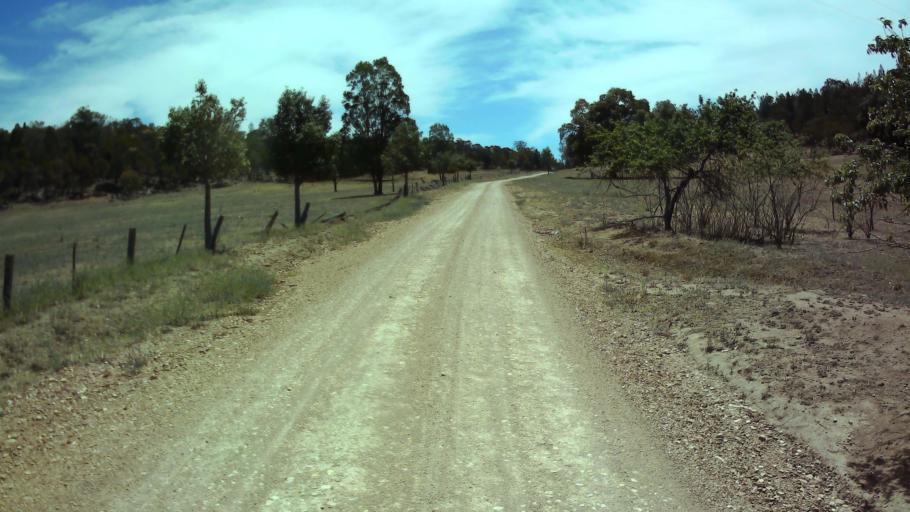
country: AU
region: New South Wales
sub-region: Weddin
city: Grenfell
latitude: -33.7477
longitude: 148.1844
